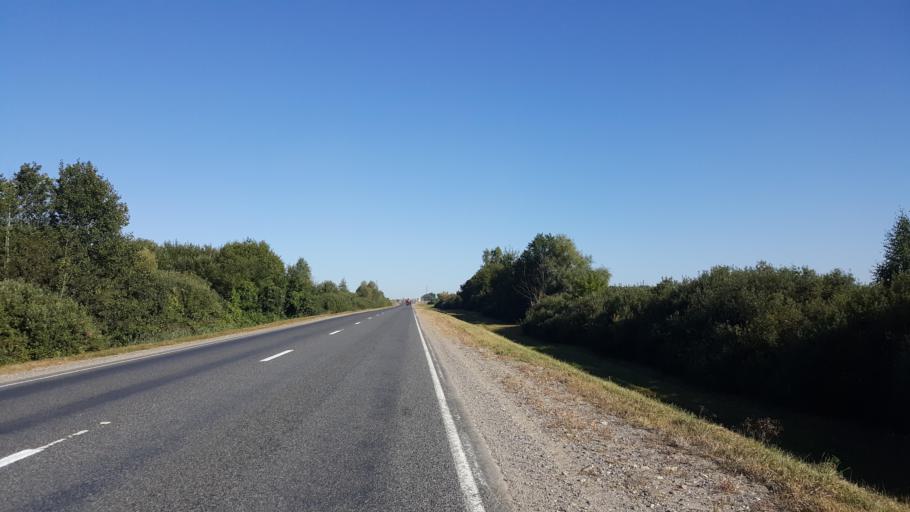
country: BY
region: Brest
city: Kamyanyets
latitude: 52.3918
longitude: 23.7863
